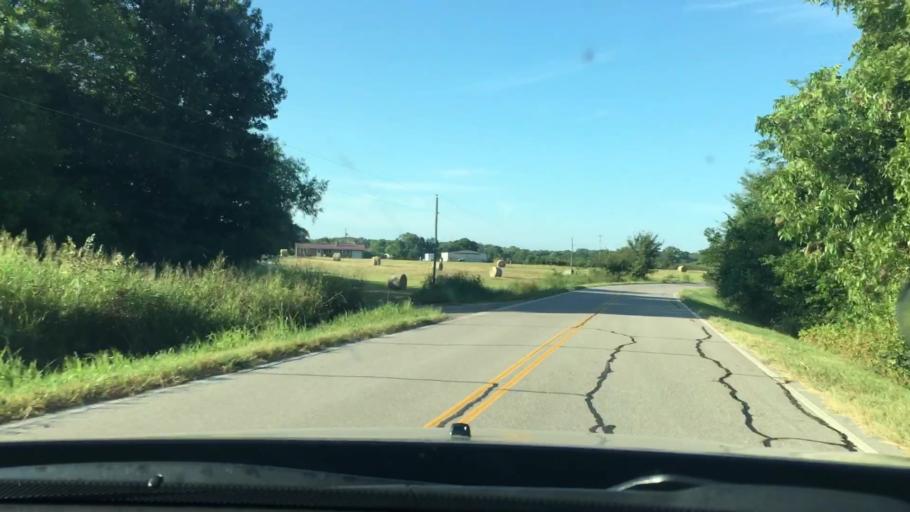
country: US
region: Oklahoma
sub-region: Pontotoc County
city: Ada
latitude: 34.6968
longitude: -96.4415
